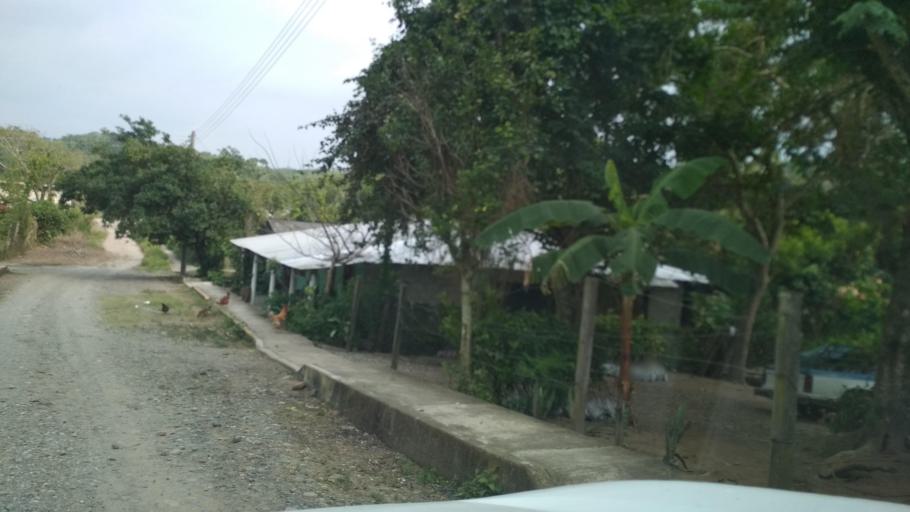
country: MM
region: Kayah
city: Loikaw
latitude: 20.2358
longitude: 97.2775
